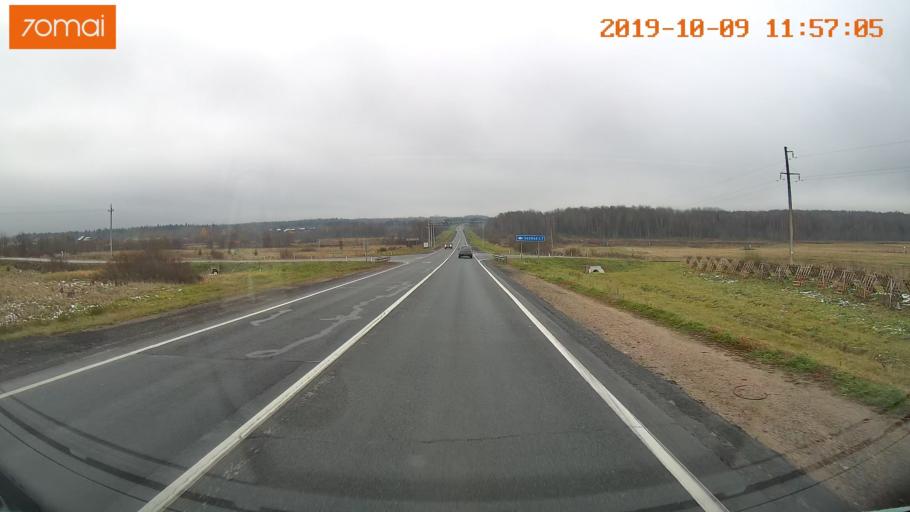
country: RU
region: Vologda
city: Gryazovets
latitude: 58.7367
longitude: 40.2907
